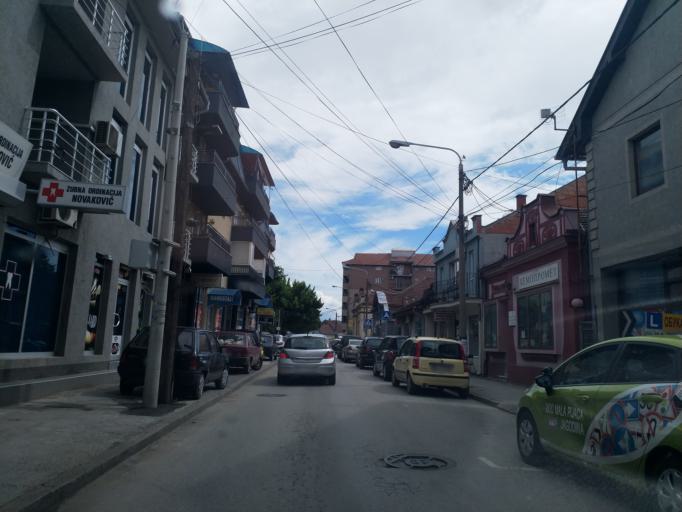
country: RS
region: Central Serbia
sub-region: Pomoravski Okrug
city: Jagodina
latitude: 43.9792
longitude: 21.2576
